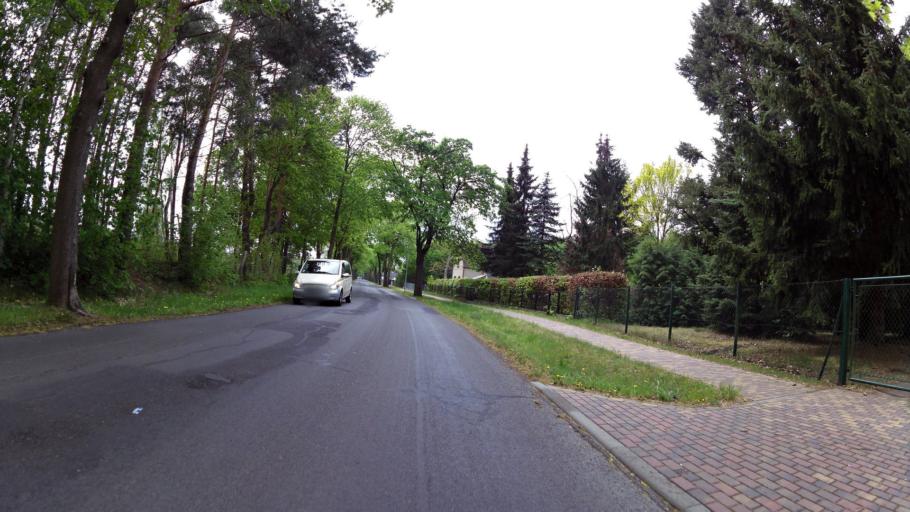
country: DE
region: Brandenburg
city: Bestensee
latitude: 52.2111
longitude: 13.5932
